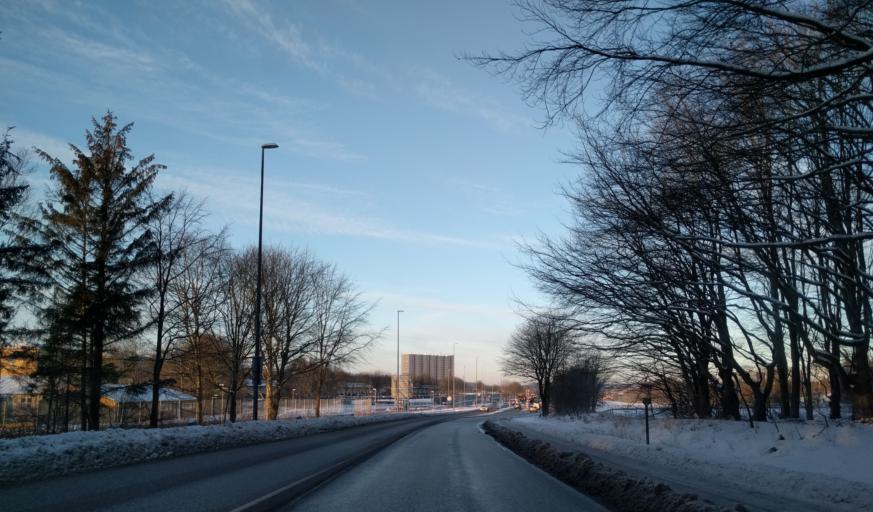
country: DK
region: North Denmark
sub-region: Alborg Kommune
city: Gistrup
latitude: 57.0204
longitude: 9.9553
